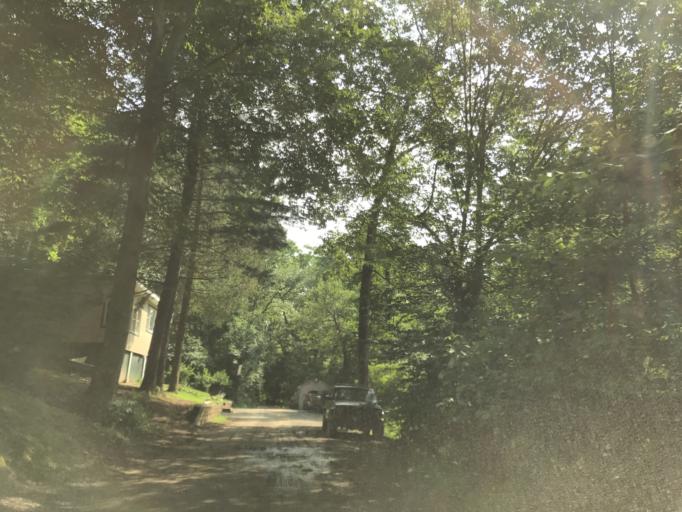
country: US
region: Pennsylvania
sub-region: York County
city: Susquehanna Trails
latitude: 39.7597
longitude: -76.2285
